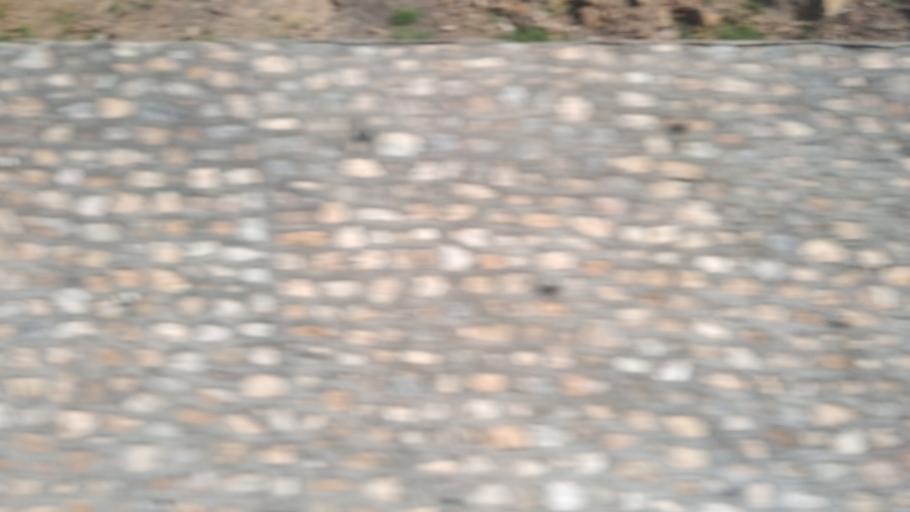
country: TR
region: Bitlis
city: Resadiye
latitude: 38.4739
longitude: 42.5134
